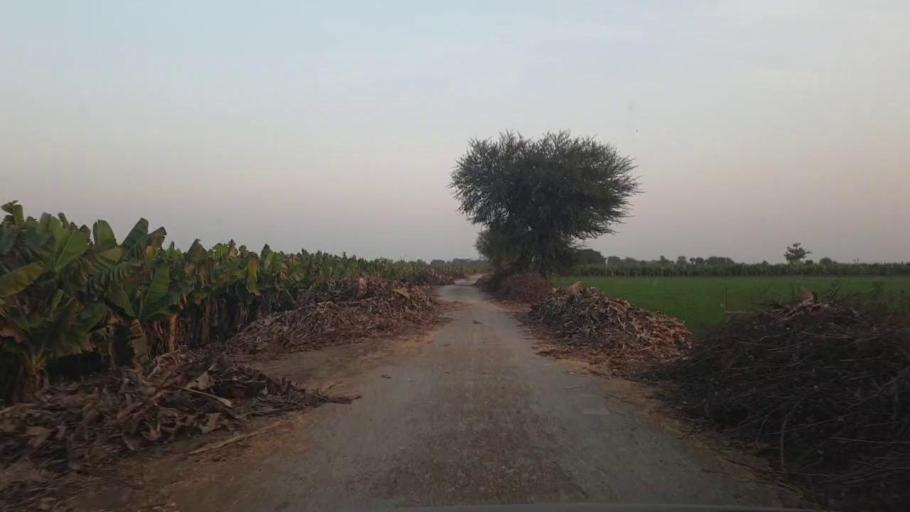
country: PK
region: Sindh
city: Bhit Shah
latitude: 25.8456
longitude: 68.5233
